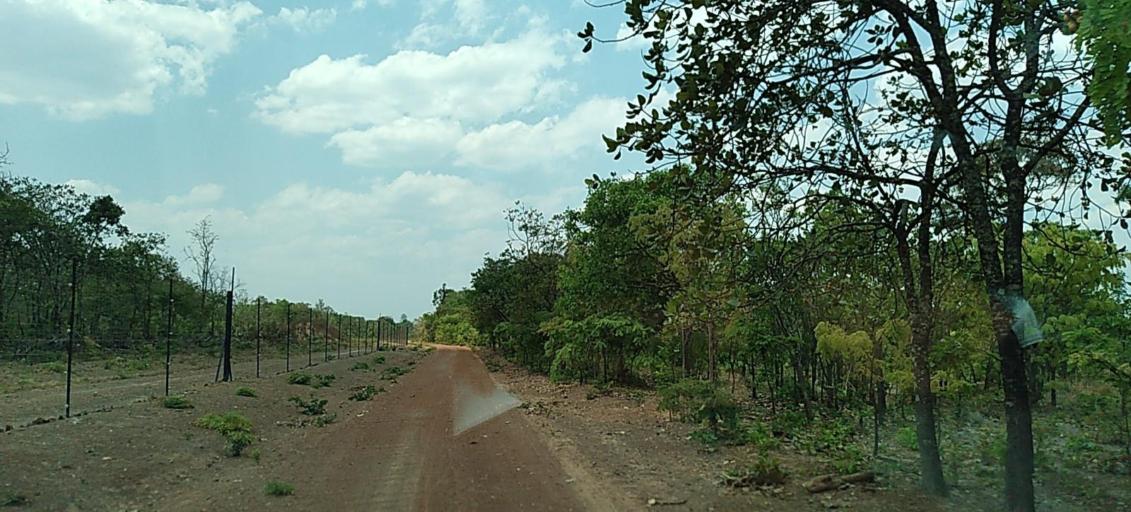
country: ZM
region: Copperbelt
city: Chililabombwe
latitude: -12.5224
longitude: 27.6252
